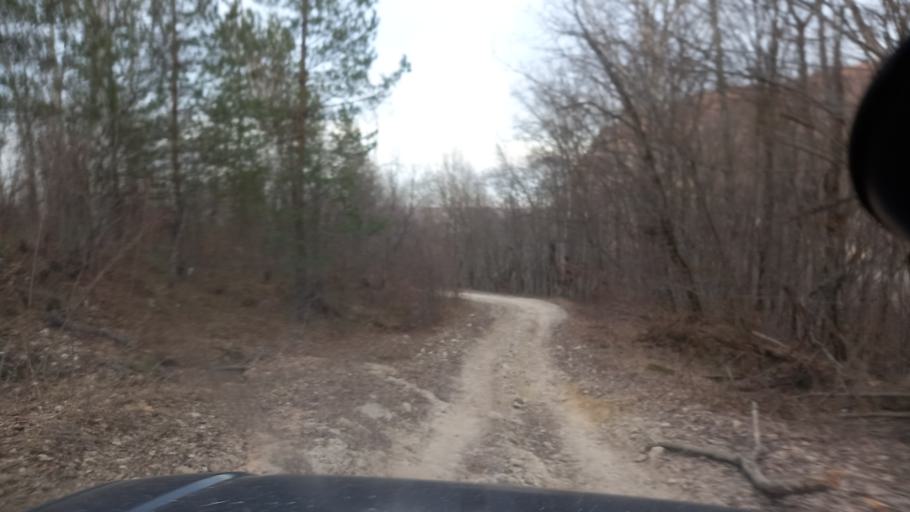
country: RU
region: Krasnodarskiy
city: Neftegorsk
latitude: 44.2197
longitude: 39.9040
